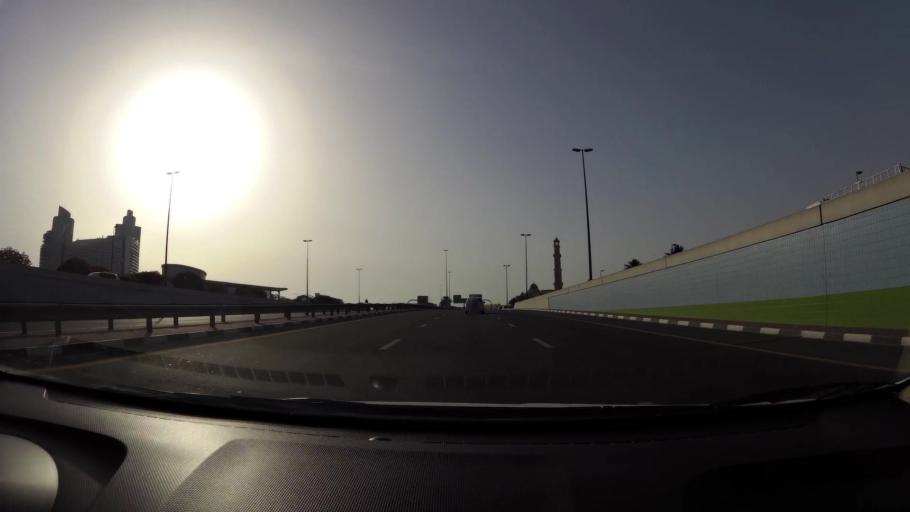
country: AE
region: Ash Shariqah
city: Sharjah
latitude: 25.2316
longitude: 55.3520
